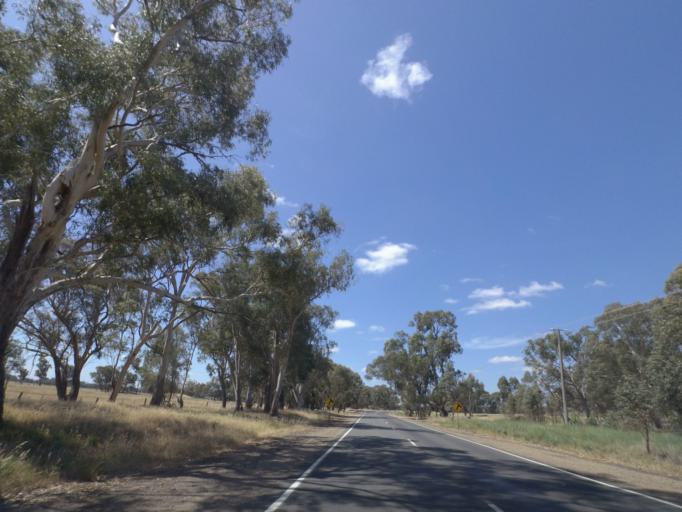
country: AU
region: Victoria
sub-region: Wangaratta
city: Wangaratta
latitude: -36.4084
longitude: 146.2709
